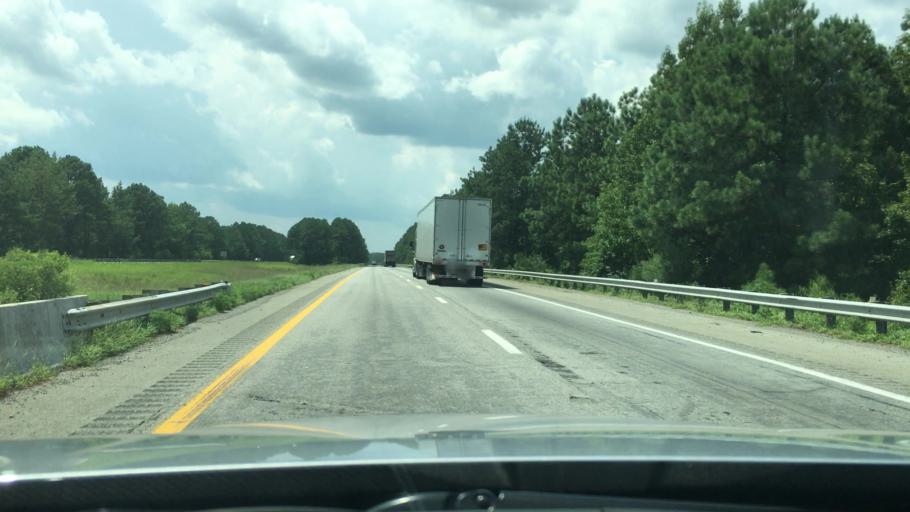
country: US
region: Virginia
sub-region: City of Emporia
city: Emporia
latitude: 36.7670
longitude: -77.4738
